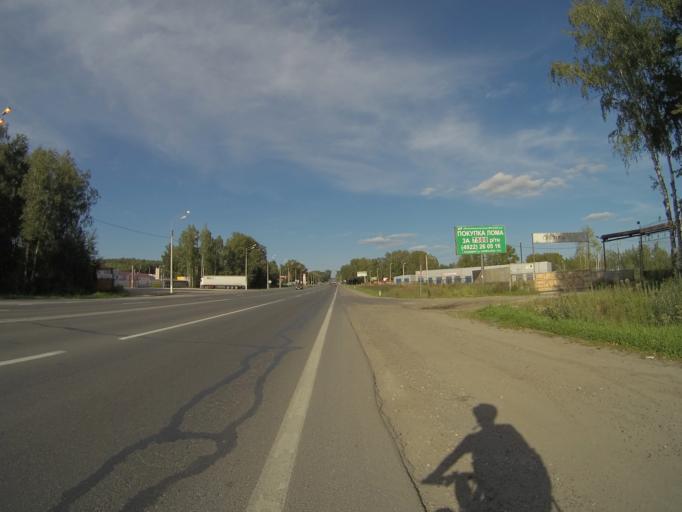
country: RU
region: Vladimir
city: Raduzhnyy
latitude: 56.0906
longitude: 40.2351
